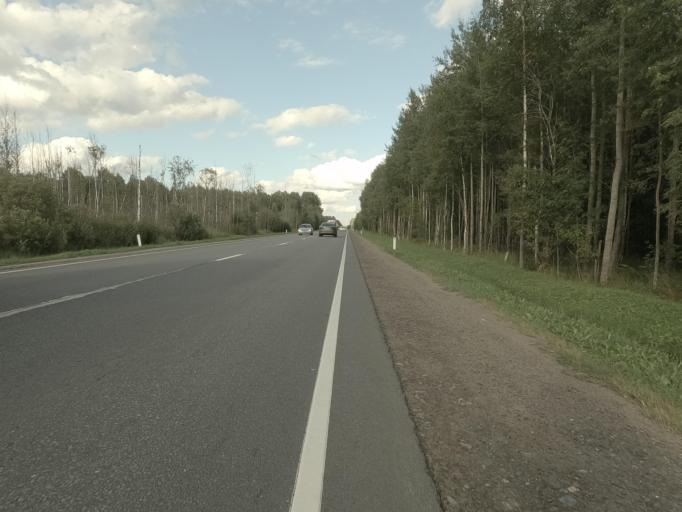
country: RU
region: Leningrad
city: Mga
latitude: 59.6833
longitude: 30.9558
